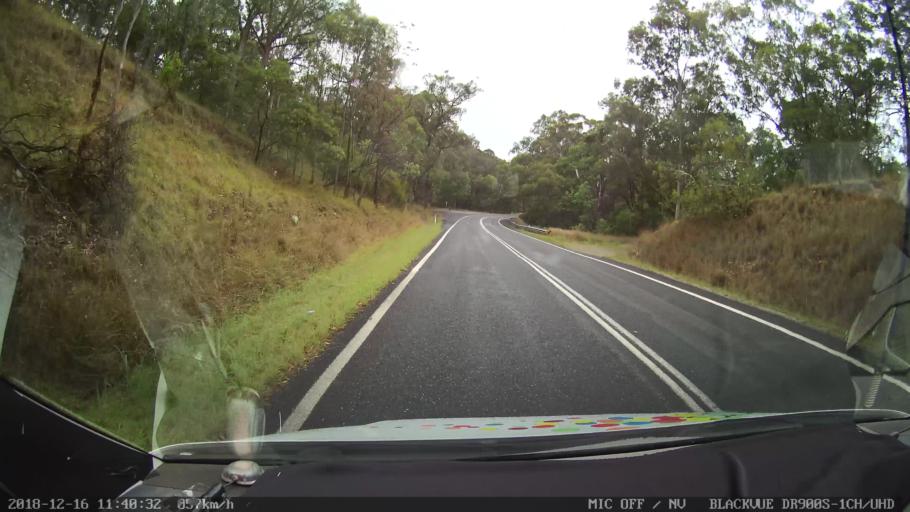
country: AU
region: New South Wales
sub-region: Tenterfield Municipality
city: Carrolls Creek
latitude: -28.9607
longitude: 152.1997
